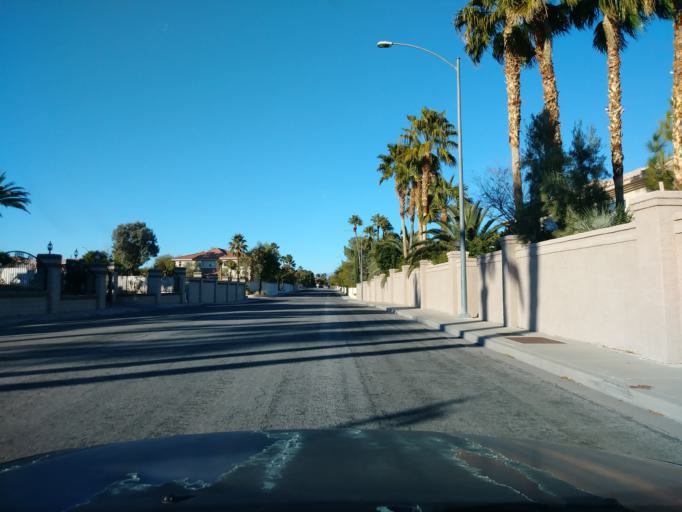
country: US
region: Nevada
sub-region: Clark County
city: Spring Valley
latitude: 36.1486
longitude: -115.2681
